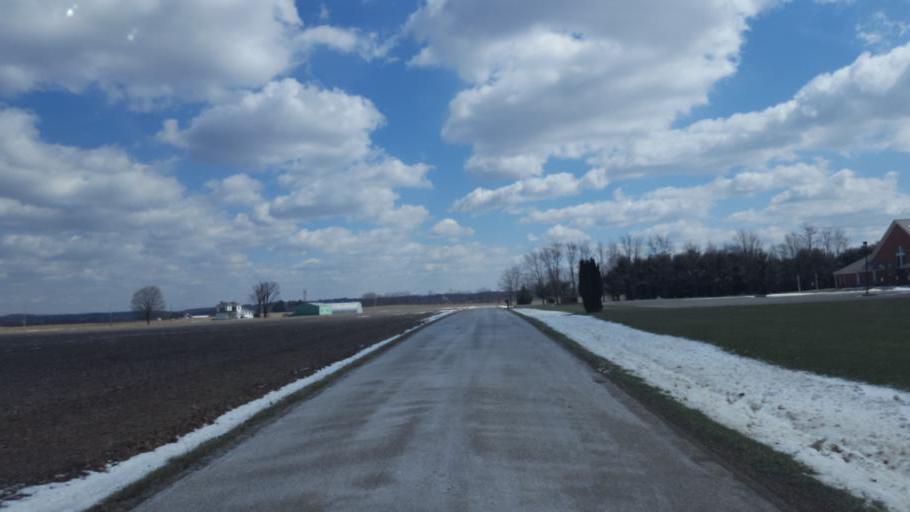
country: US
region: Ohio
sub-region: Knox County
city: Mount Vernon
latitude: 40.3540
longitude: -82.5158
